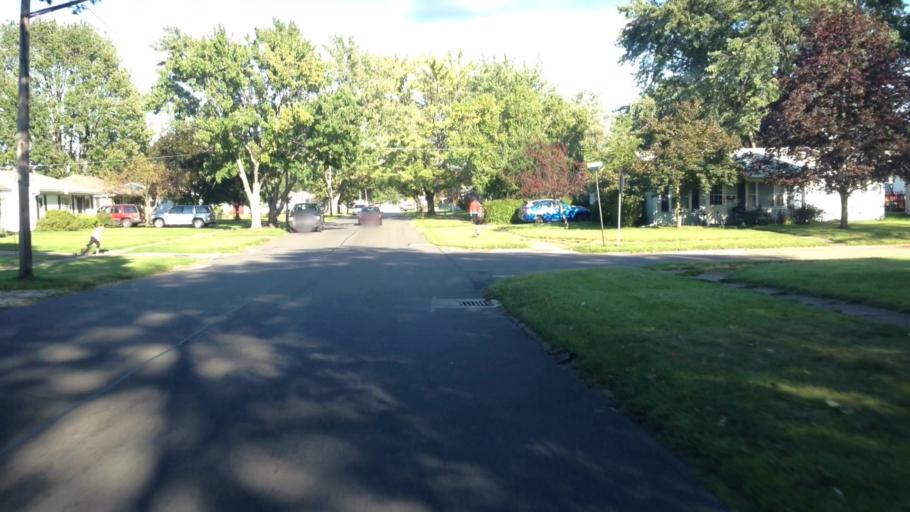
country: US
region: Ohio
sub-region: Lorain County
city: Elyria
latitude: 41.3850
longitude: -82.1139
